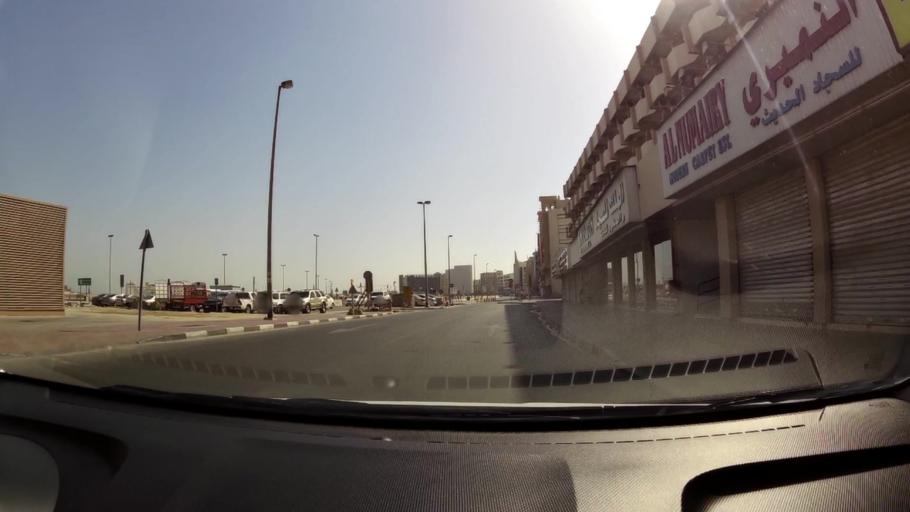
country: AE
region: Ash Shariqah
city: Sharjah
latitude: 25.2692
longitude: 55.2946
